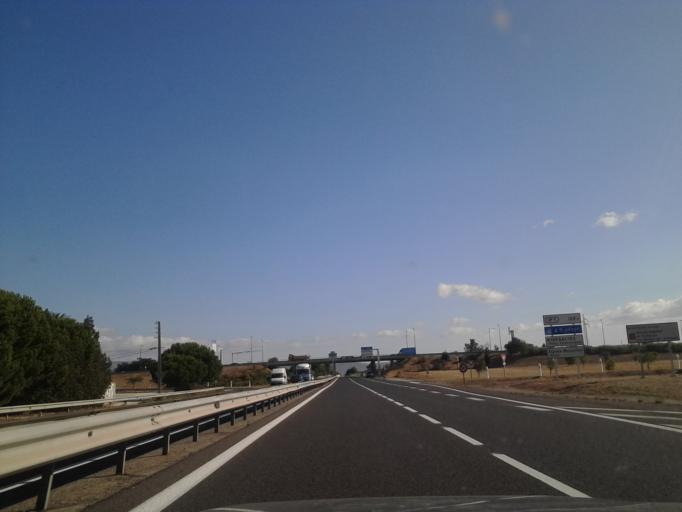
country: FR
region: Languedoc-Roussillon
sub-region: Departement des Pyrenees-Orientales
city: Rivesaltes
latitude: 42.7770
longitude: 2.9028
